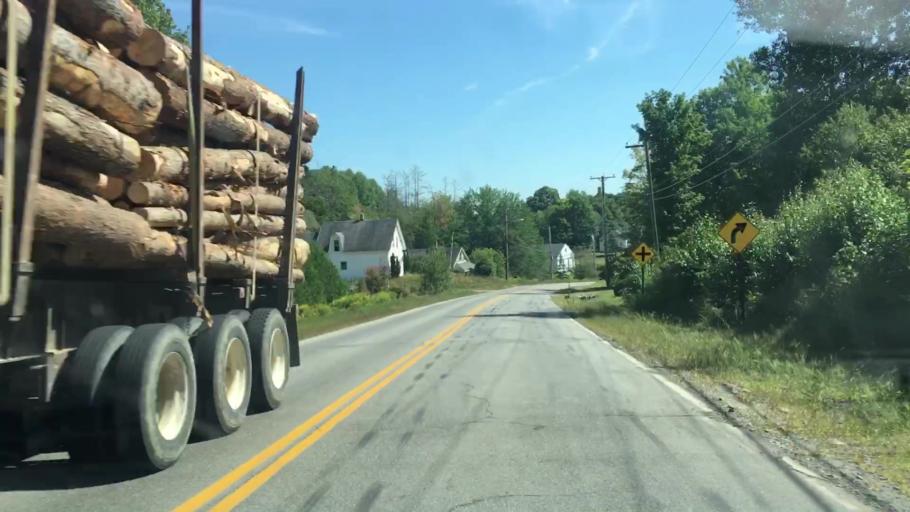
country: US
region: Maine
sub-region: Penobscot County
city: Bradford
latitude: 45.1698
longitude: -68.8481
